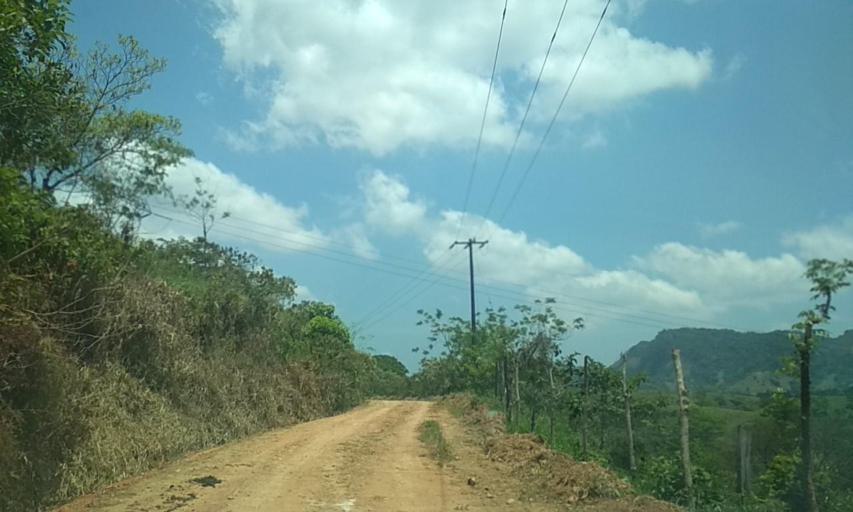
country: MX
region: Chiapas
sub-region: Tecpatan
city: Raudales Malpaso
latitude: 17.3917
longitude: -93.7364
